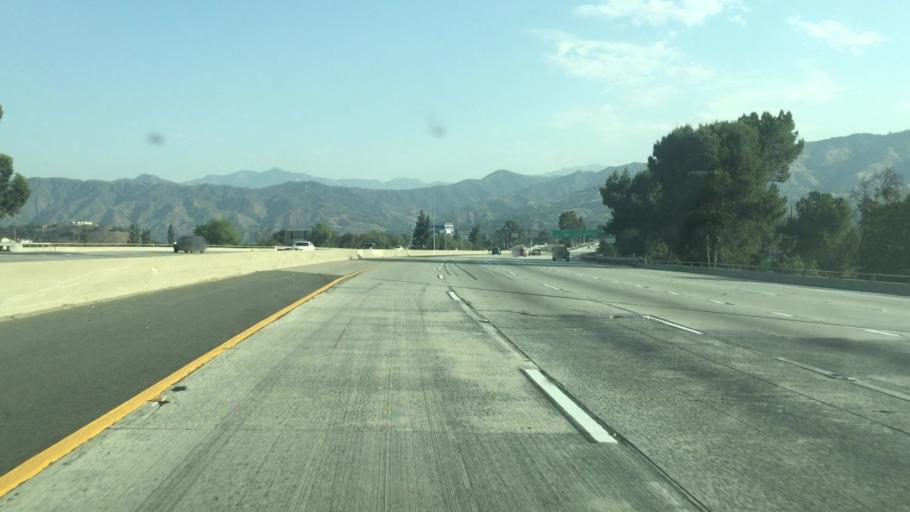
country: US
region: California
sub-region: Los Angeles County
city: San Dimas
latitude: 34.1109
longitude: -117.8237
